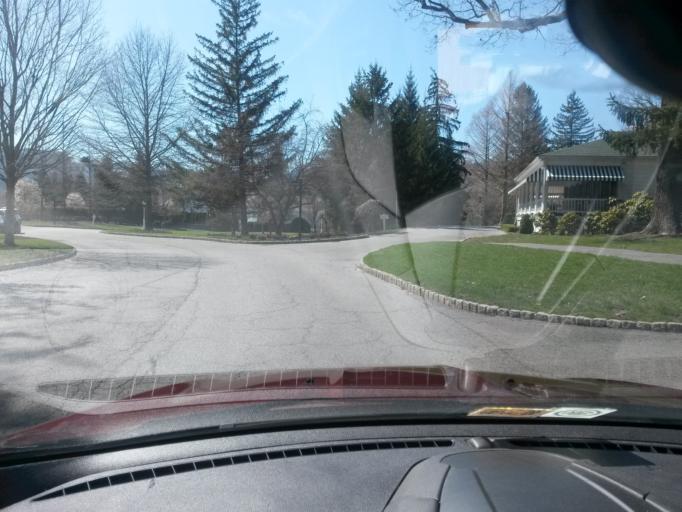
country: US
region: West Virginia
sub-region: Greenbrier County
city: White Sulphur Springs
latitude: 37.7874
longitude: -80.3059
